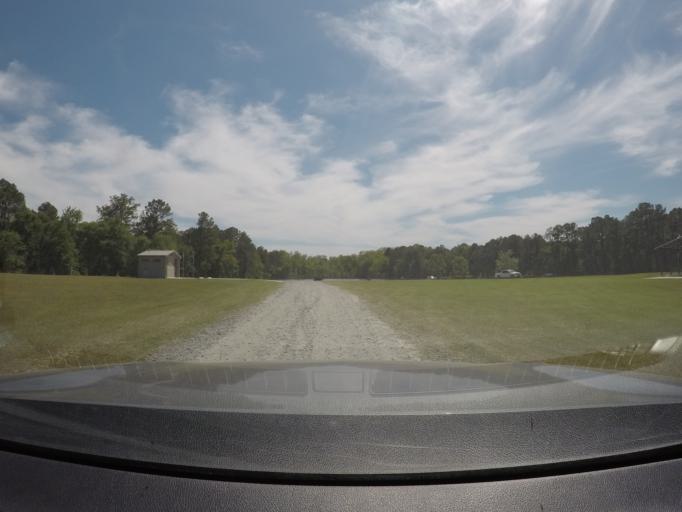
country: US
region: Georgia
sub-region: Evans County
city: Claxton
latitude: 32.1234
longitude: -81.8036
